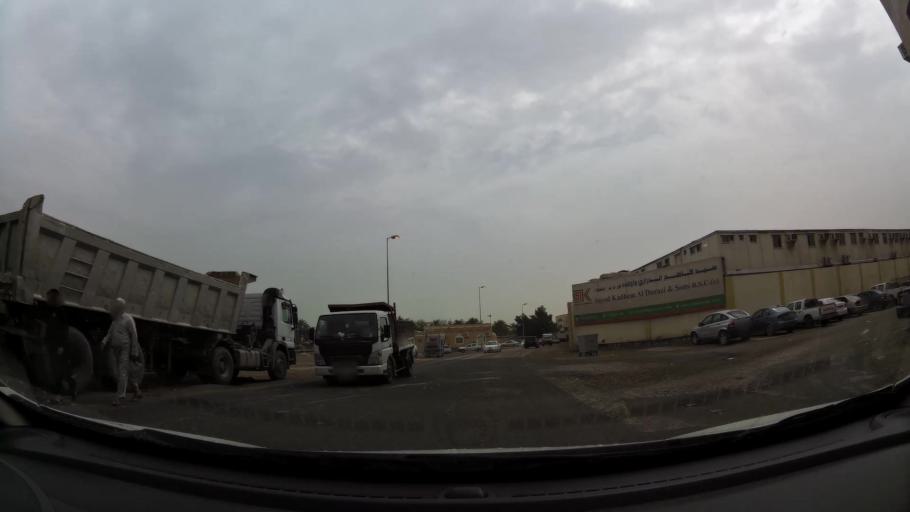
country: BH
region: Northern
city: Ar Rifa'
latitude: 26.1375
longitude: 50.5888
